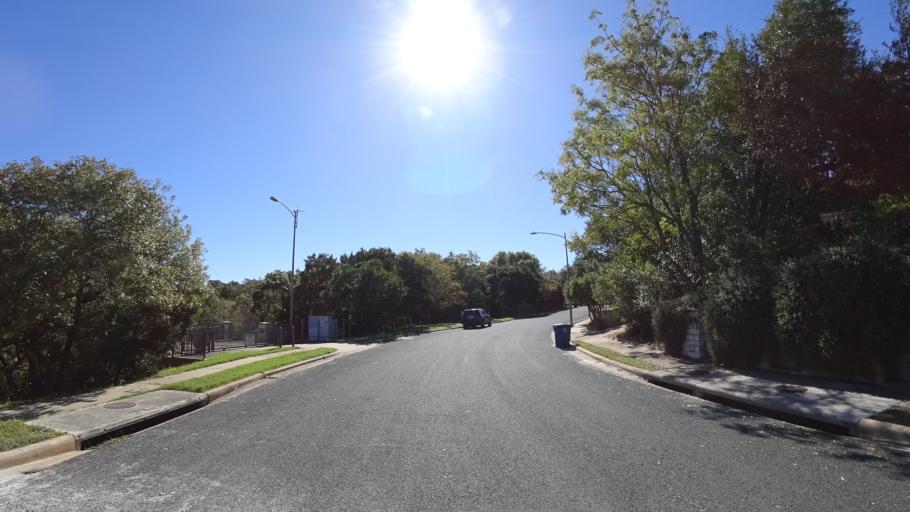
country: US
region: Texas
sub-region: Travis County
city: West Lake Hills
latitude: 30.3531
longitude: -97.7767
